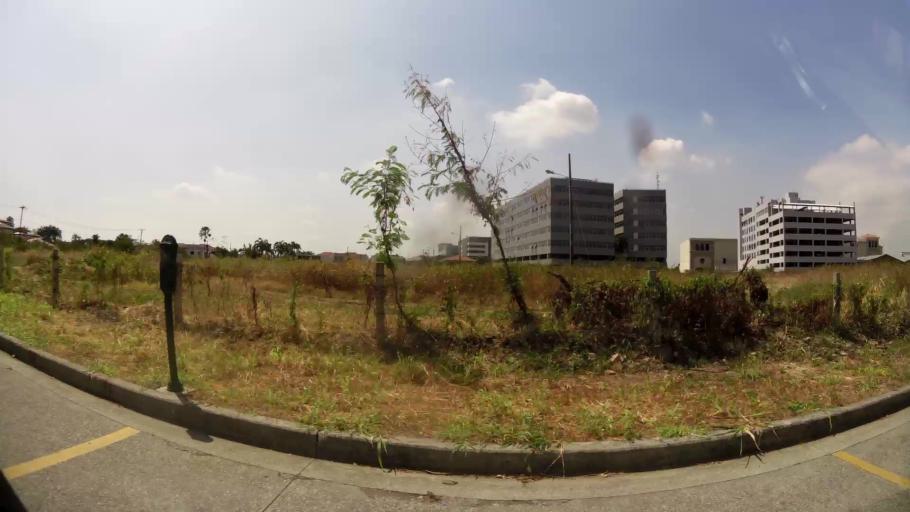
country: EC
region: Guayas
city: Eloy Alfaro
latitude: -2.1386
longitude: -79.8679
